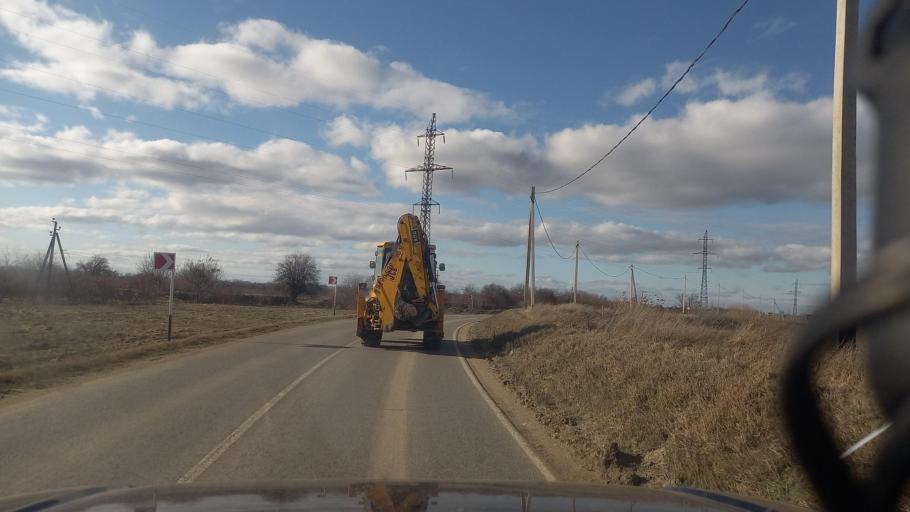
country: RU
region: Adygeya
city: Yablonovskiy
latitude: 45.0185
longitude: 38.9022
